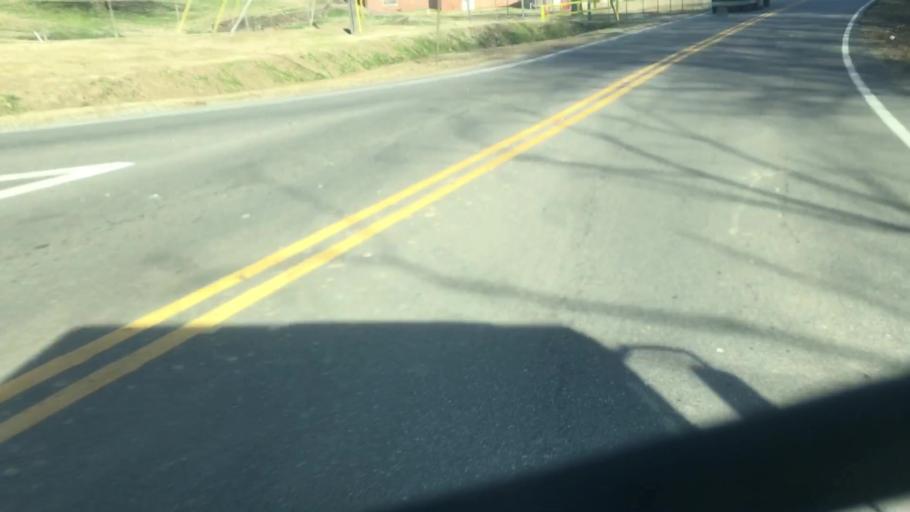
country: US
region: Alabama
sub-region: Jefferson County
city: Cahaba Heights
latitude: 33.4510
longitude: -86.7176
